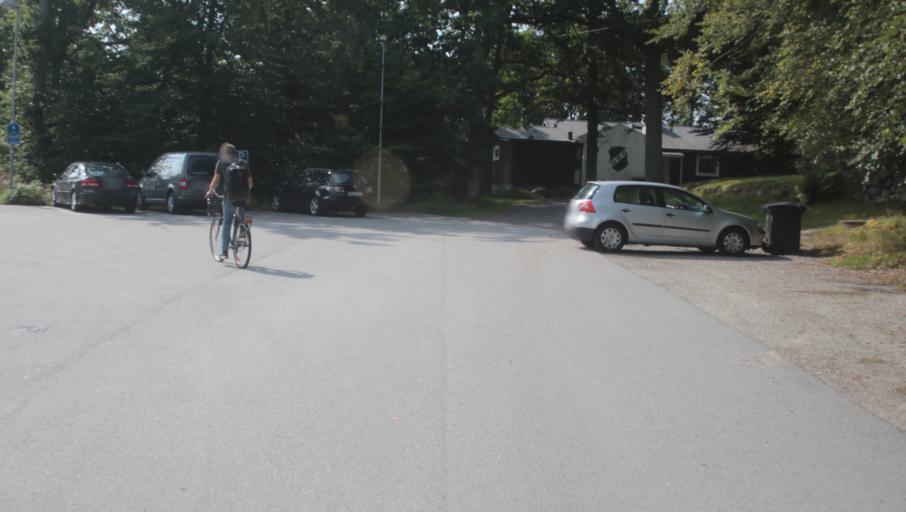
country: SE
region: Blekinge
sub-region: Karlshamns Kommun
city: Karlshamn
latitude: 56.1660
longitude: 14.8821
